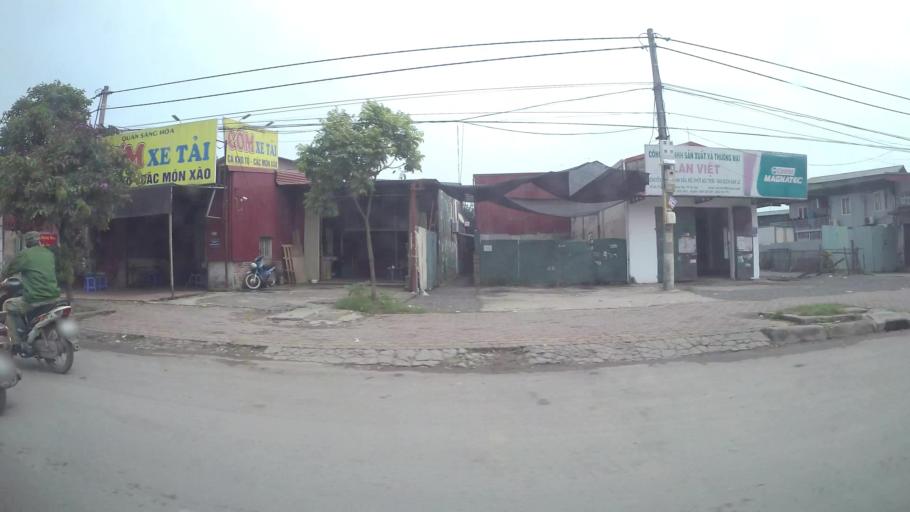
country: VN
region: Ha Noi
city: Van Dien
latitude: 20.9644
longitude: 105.8604
